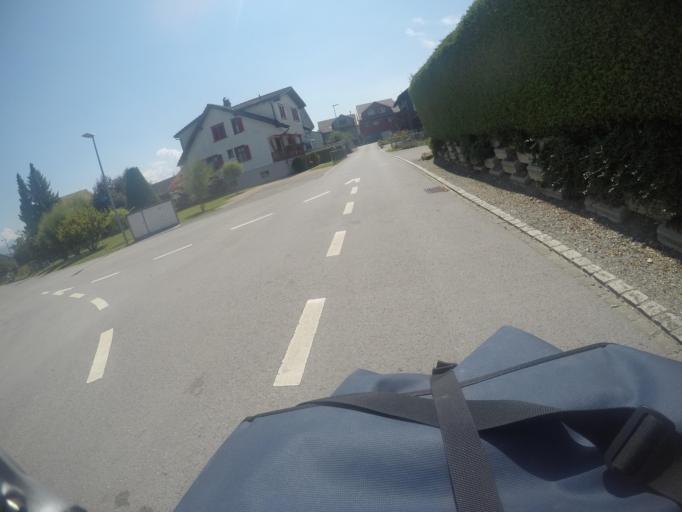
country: CH
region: Saint Gallen
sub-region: Wahlkreis Rheintal
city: Altstatten
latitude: 47.3736
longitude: 9.5580
